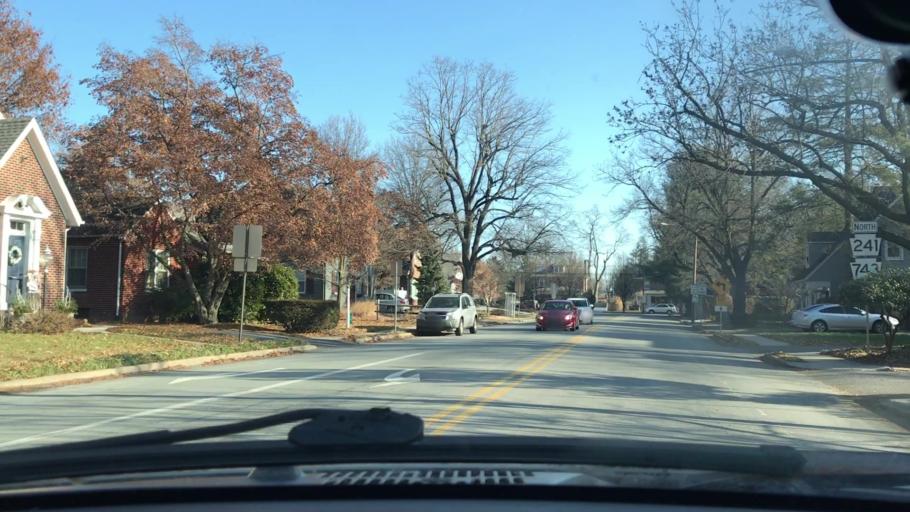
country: US
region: Pennsylvania
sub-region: Lancaster County
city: Elizabethtown
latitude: 40.1576
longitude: -76.6099
